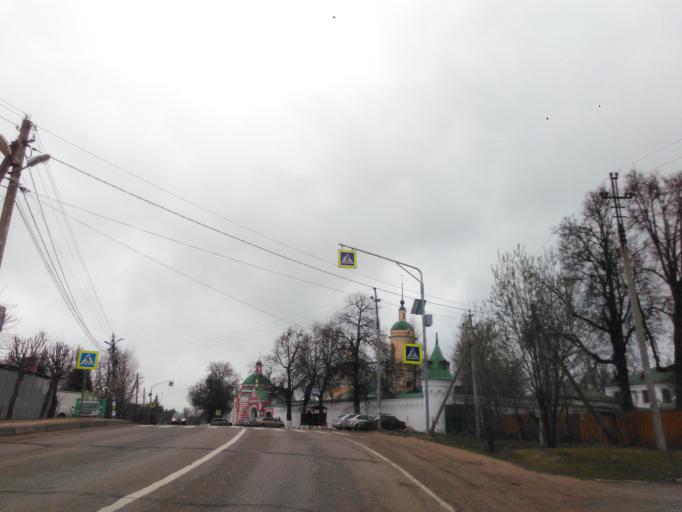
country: RU
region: Moskovskaya
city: Rozhdestveno
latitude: 55.8396
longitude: 37.0069
